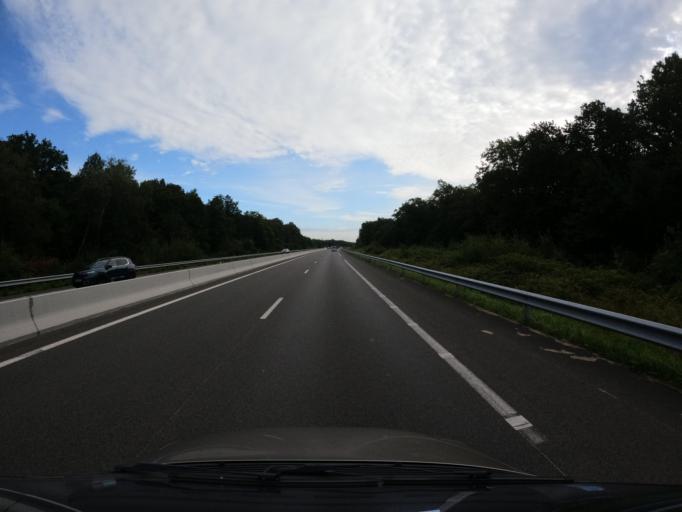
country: FR
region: Centre
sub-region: Departement d'Indre-et-Loire
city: Restigne
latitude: 47.2939
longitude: 0.2865
